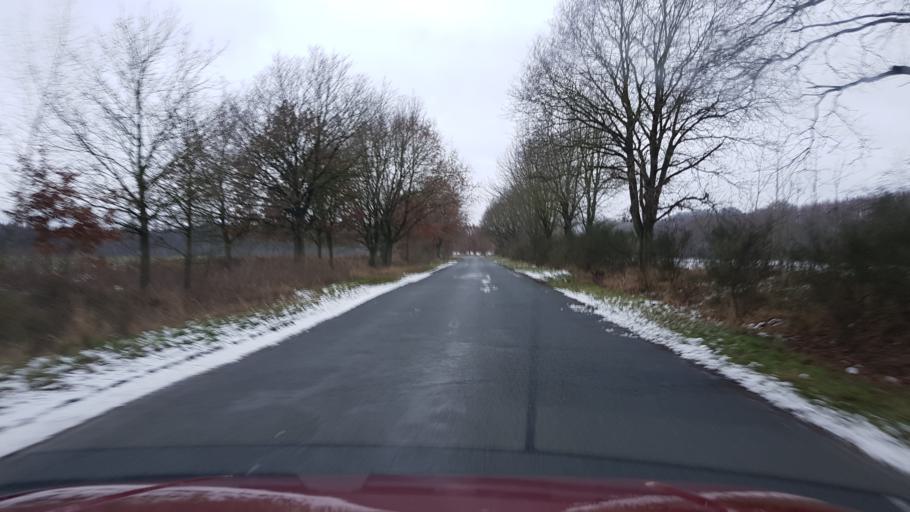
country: PL
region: West Pomeranian Voivodeship
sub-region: Powiat goleniowski
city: Nowogard
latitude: 53.6831
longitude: 15.2333
